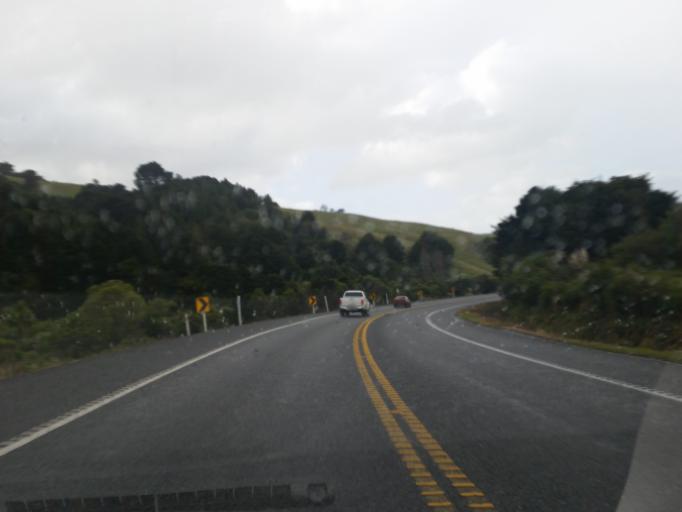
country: NZ
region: Waikato
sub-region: Hauraki District
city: Ngatea
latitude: -37.2802
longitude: 175.3248
